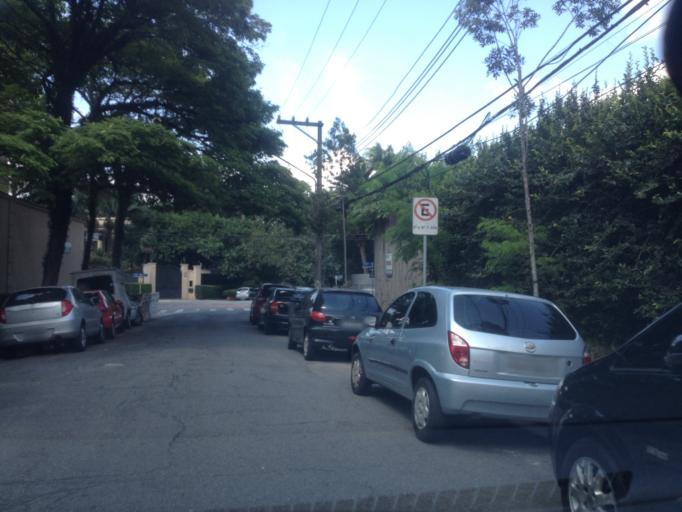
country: BR
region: Sao Paulo
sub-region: Sao Paulo
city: Sao Paulo
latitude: -23.5664
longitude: -46.6706
